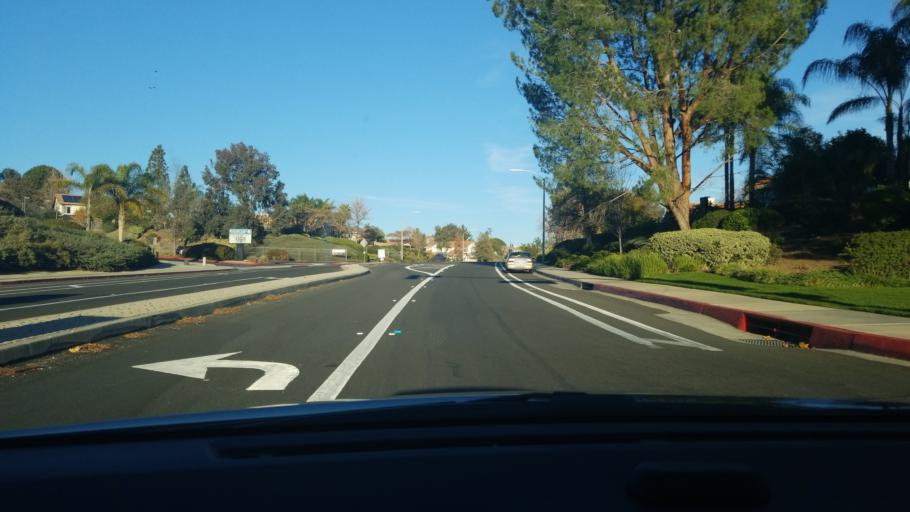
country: US
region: California
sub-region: Riverside County
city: Temecula
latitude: 33.5261
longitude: -117.1122
